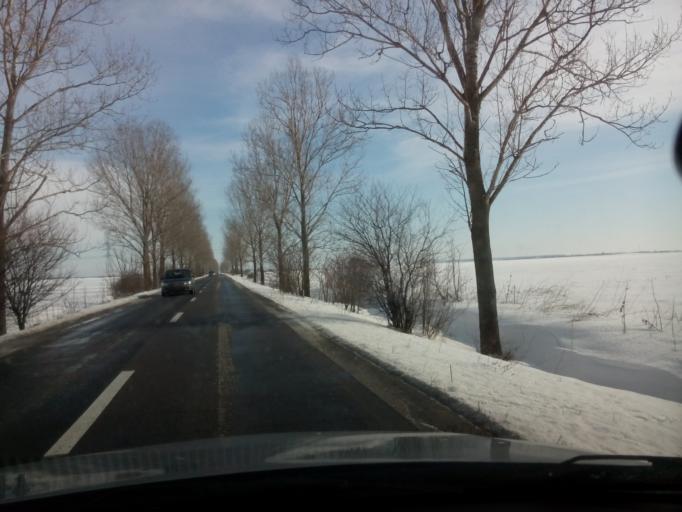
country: RO
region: Calarasi
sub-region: Comuna Luica
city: Luica
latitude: 44.2253
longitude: 26.5577
